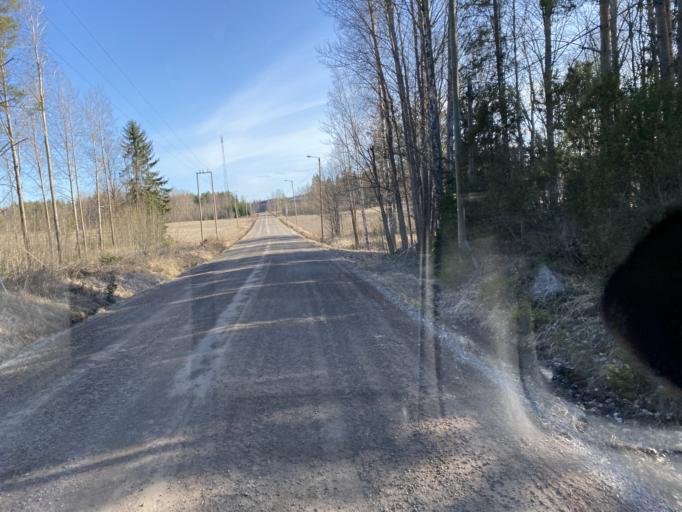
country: FI
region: Satakunta
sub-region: Rauma
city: Lappi
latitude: 61.1325
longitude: 21.9489
